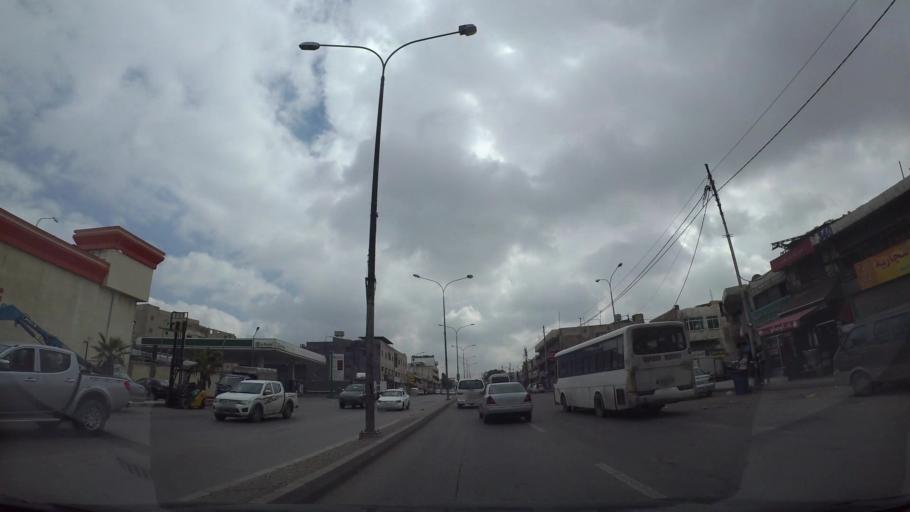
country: JO
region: Amman
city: Al Quwaysimah
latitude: 31.9186
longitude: 35.9384
